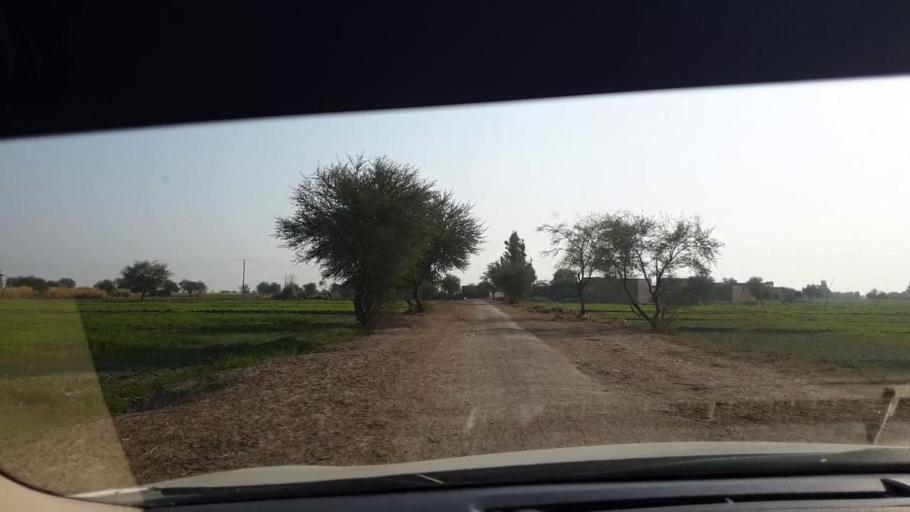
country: PK
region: Sindh
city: Berani
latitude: 25.8133
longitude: 68.7761
